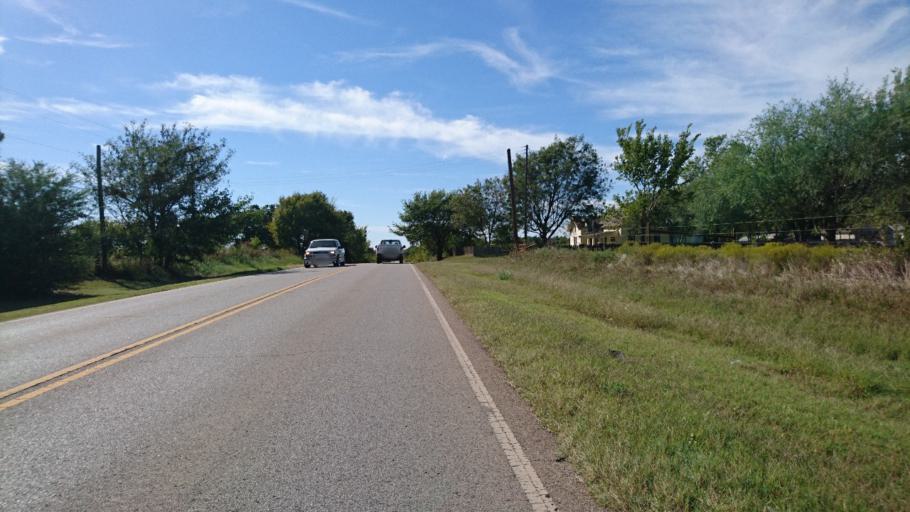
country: US
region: Oklahoma
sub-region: Lincoln County
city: Chandler
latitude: 35.7099
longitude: -96.8116
